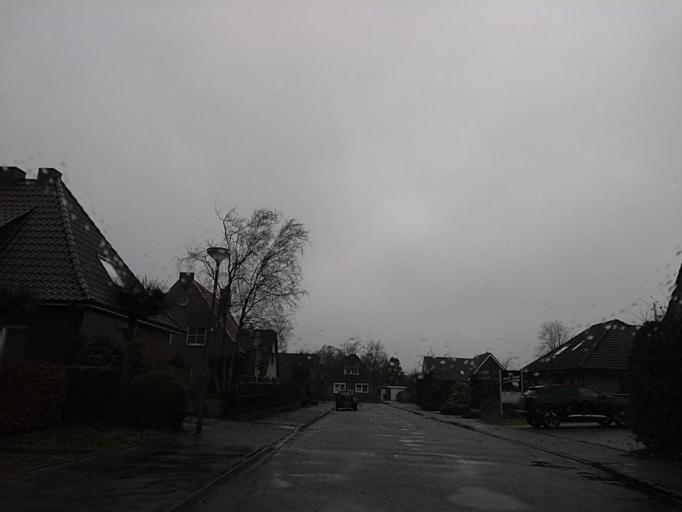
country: DE
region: Lower Saxony
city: Leer
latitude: 53.2335
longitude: 7.4837
